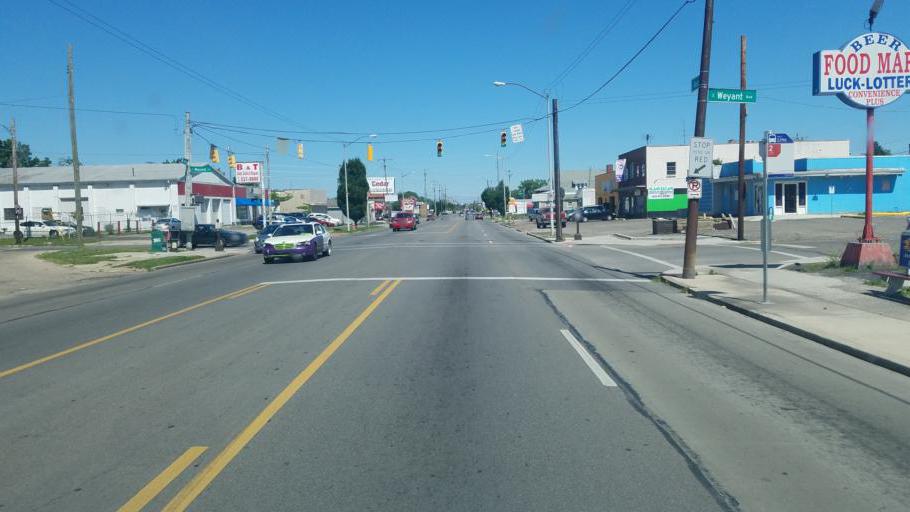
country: US
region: Ohio
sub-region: Franklin County
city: Whitehall
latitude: 39.9564
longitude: -82.9089
